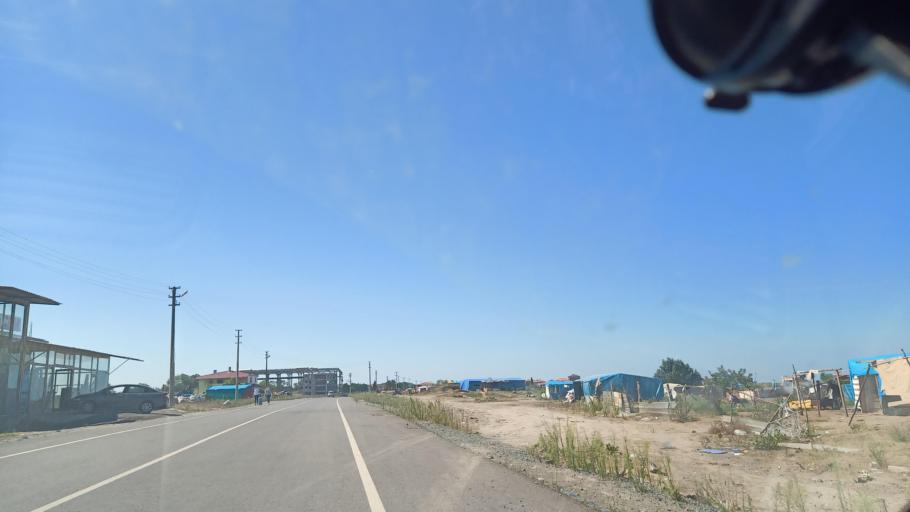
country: TR
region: Sakarya
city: Karasu
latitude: 41.1174
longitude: 30.6630
